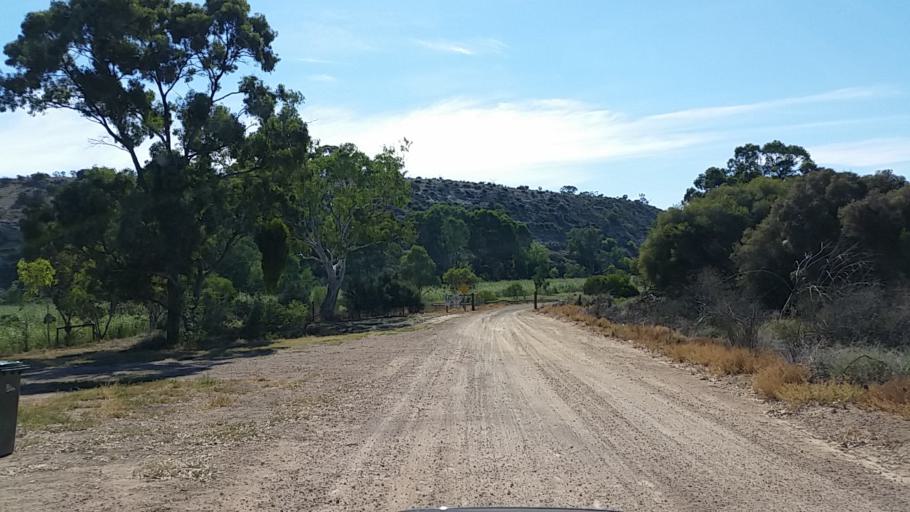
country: AU
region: South Australia
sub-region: Mid Murray
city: Mannum
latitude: -34.7014
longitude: 139.5730
